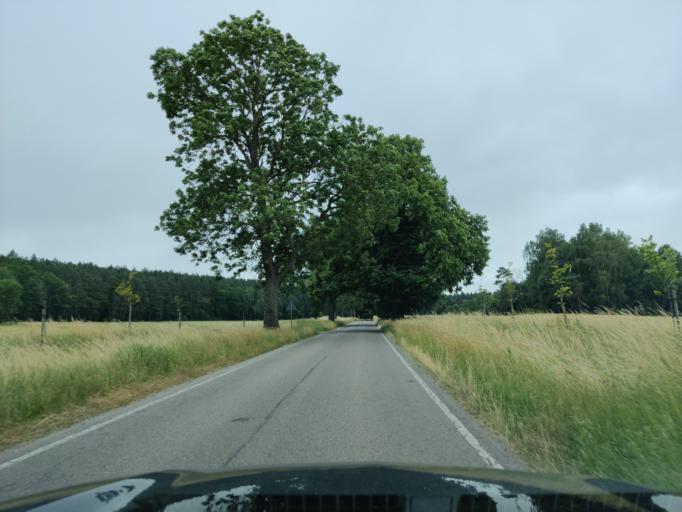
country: PL
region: Warmian-Masurian Voivodeship
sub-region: Powiat gizycki
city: Ryn
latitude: 53.8980
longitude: 21.5721
